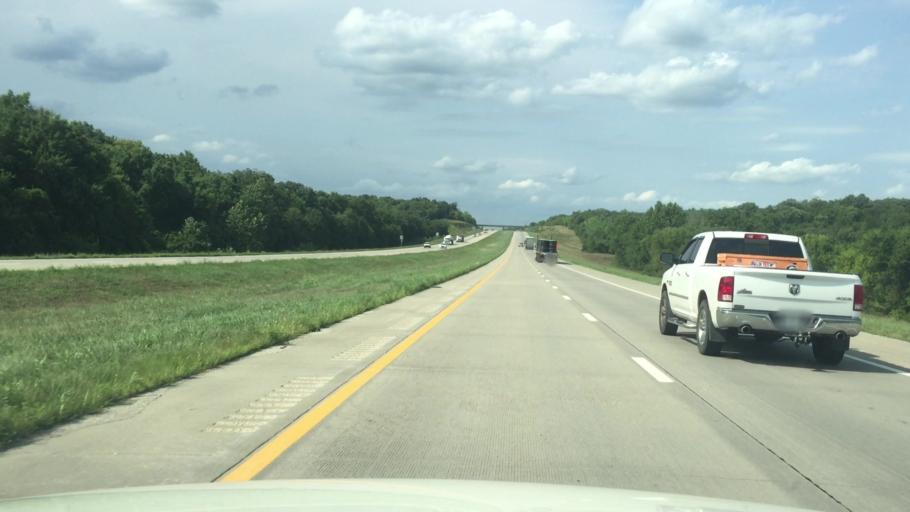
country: US
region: Kansas
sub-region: Miami County
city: Louisburg
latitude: 38.5952
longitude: -94.6940
